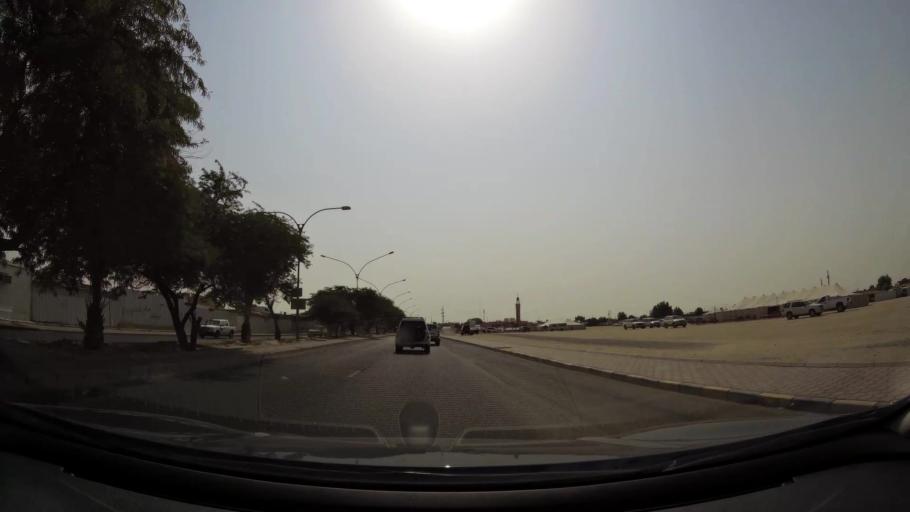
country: KW
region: Muhafazat al Jahra'
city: Al Jahra'
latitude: 29.3328
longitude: 47.6827
